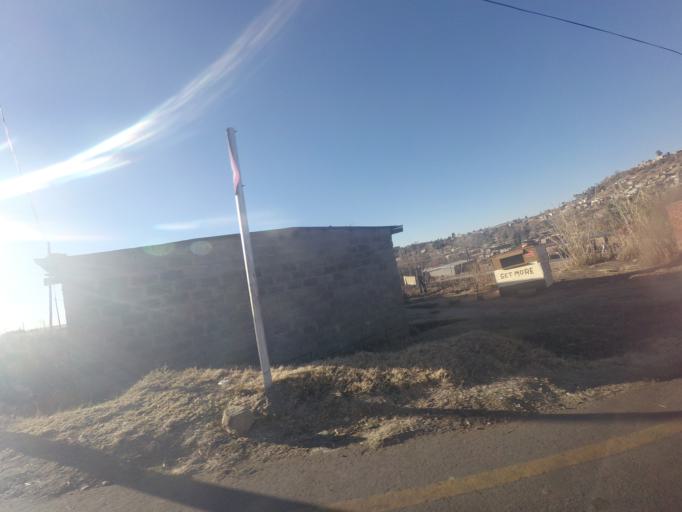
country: LS
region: Maseru
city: Maseru
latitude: -29.3250
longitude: 27.5159
